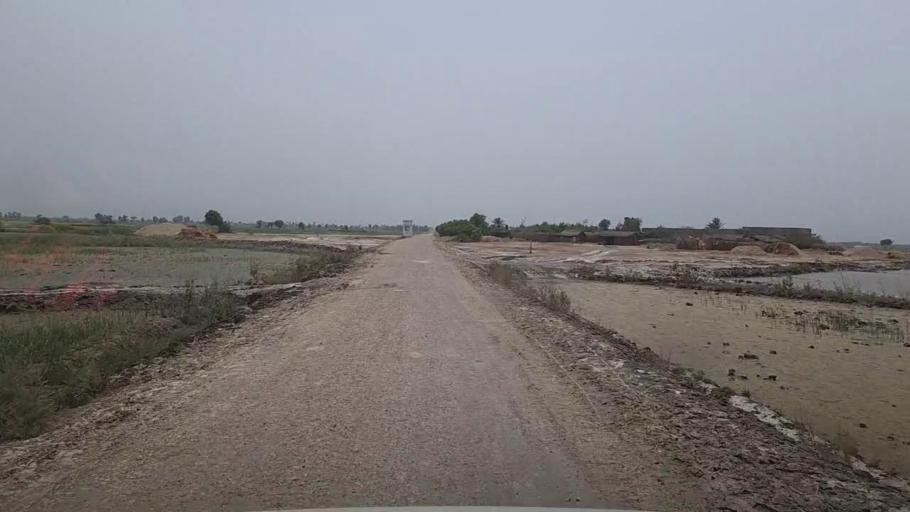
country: PK
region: Sindh
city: Sita Road
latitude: 27.0642
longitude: 67.8593
